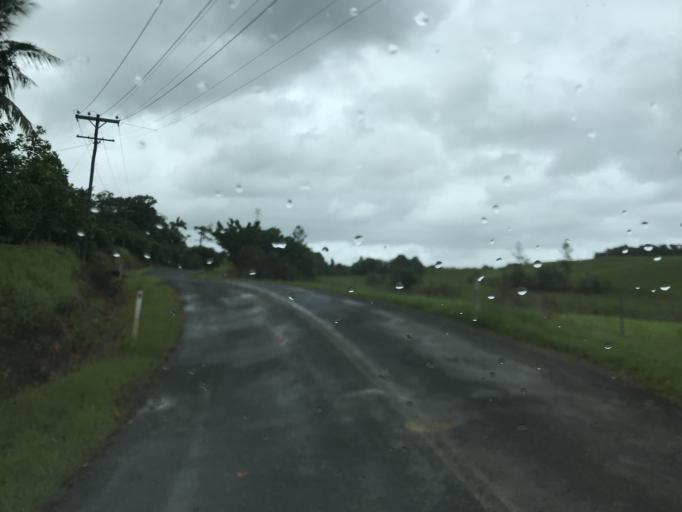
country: AU
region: Queensland
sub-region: Cassowary Coast
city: Innisfail
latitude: -17.5153
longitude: 145.9757
